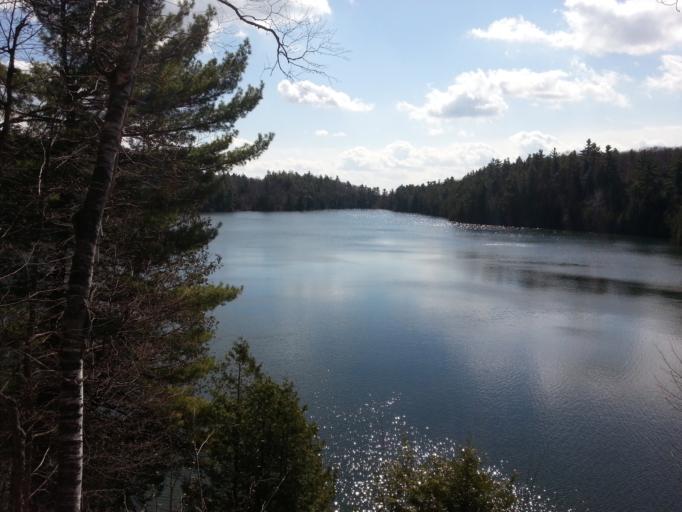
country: CA
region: Quebec
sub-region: Outaouais
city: Gatineau
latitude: 45.4688
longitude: -75.8113
